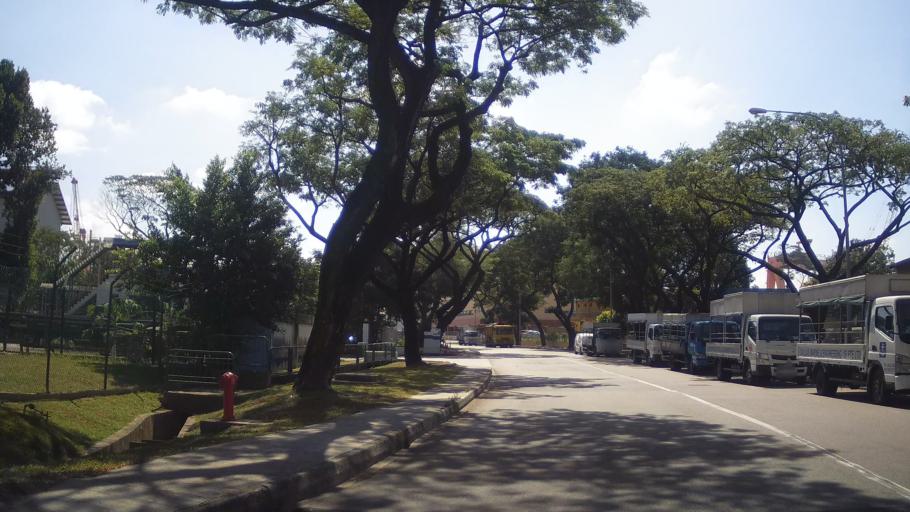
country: SG
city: Singapore
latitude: 1.3053
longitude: 103.7021
